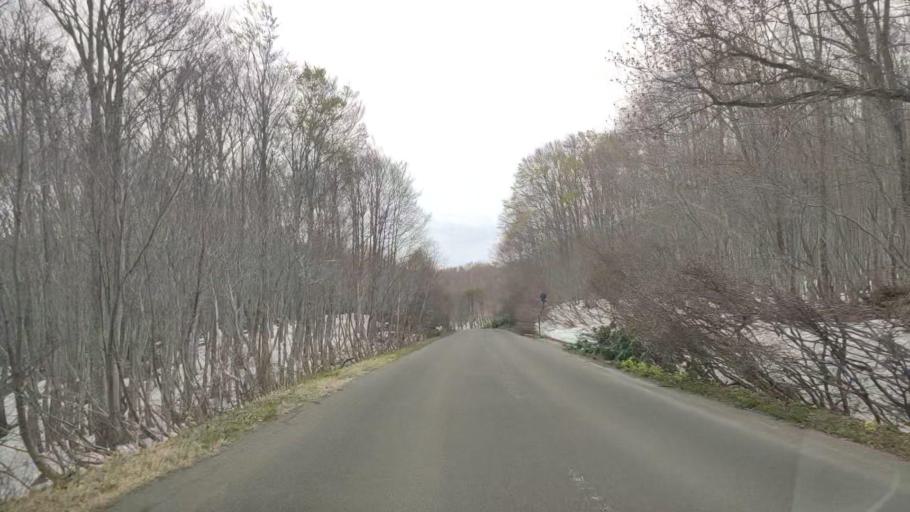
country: JP
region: Aomori
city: Aomori Shi
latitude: 40.6892
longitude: 140.9173
